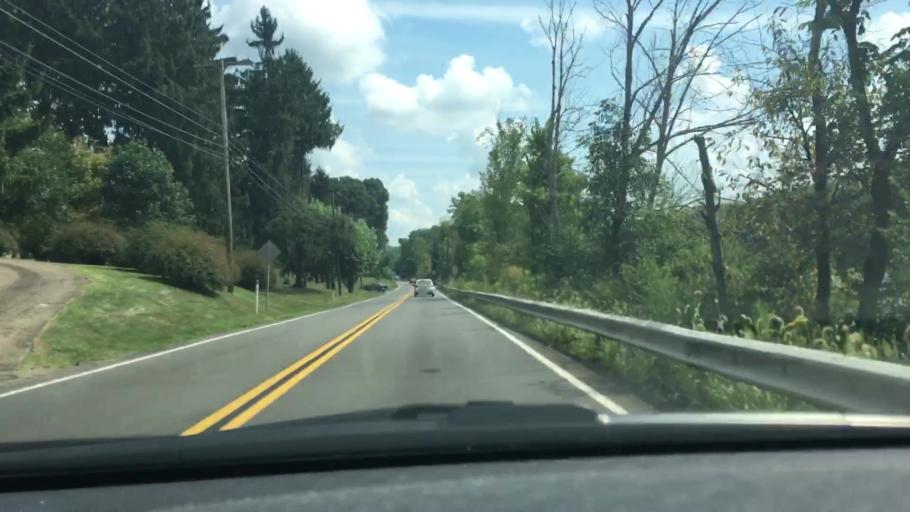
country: US
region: Pennsylvania
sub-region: Washington County
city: Thompsonville
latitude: 40.2555
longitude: -80.1282
